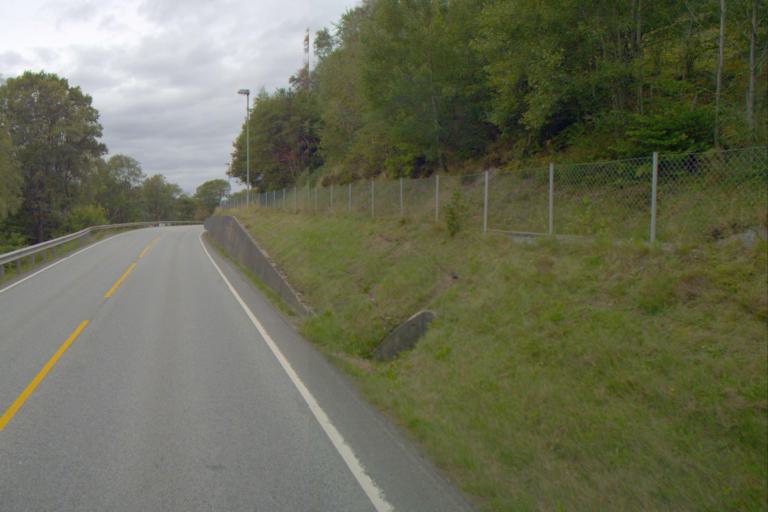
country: NO
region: Rogaland
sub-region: Sandnes
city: Hommersak
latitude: 58.8709
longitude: 5.8070
